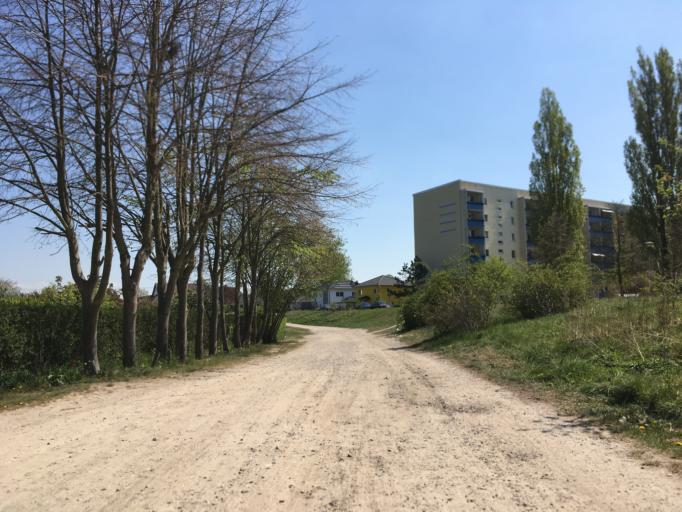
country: DE
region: Brandenburg
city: Bernau bei Berlin
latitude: 52.6724
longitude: 13.5577
